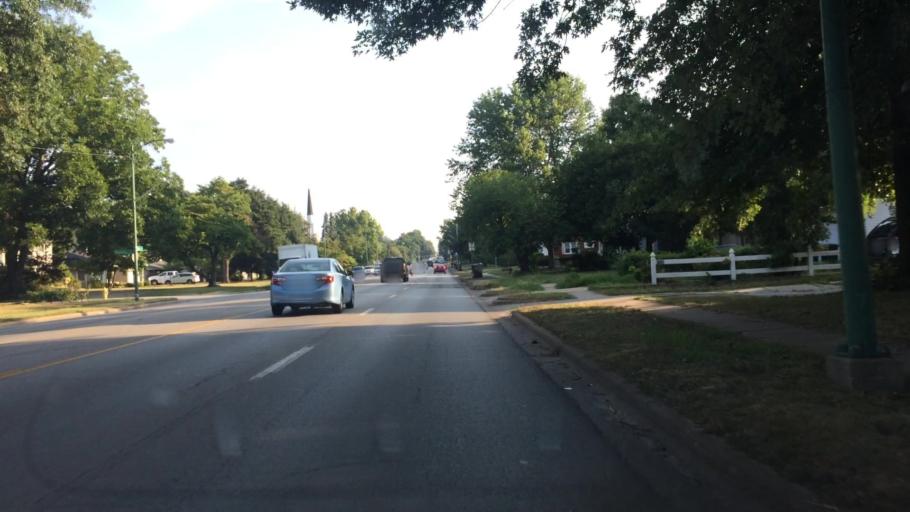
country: US
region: Missouri
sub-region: Greene County
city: Springfield
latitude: 37.1830
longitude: -93.2766
